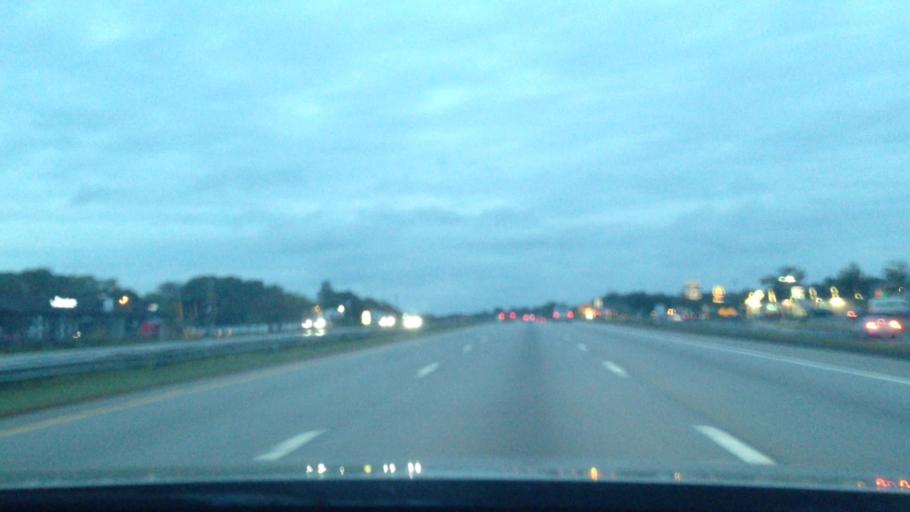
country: US
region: New York
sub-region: Suffolk County
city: Bohemia
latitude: 40.7529
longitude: -73.1214
